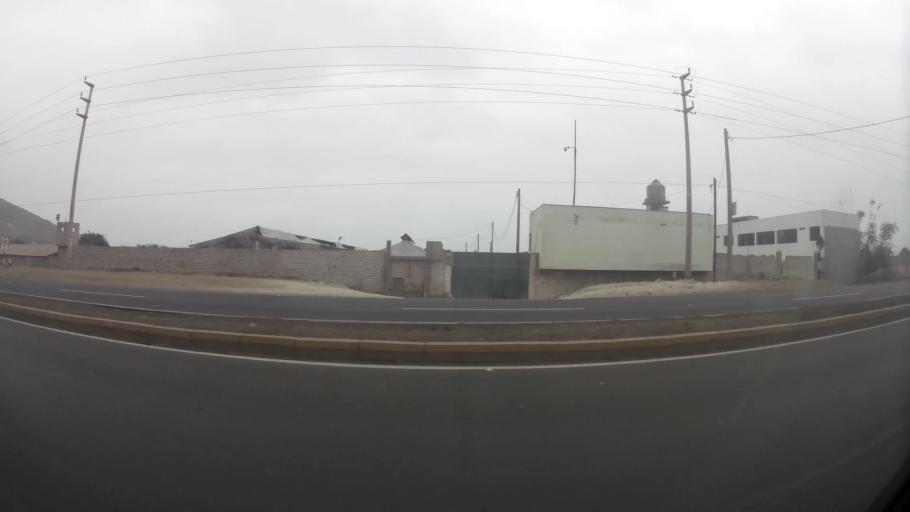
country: PE
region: Lima
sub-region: Provincia de Huaral
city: Chancay
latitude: -11.5741
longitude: -77.2630
